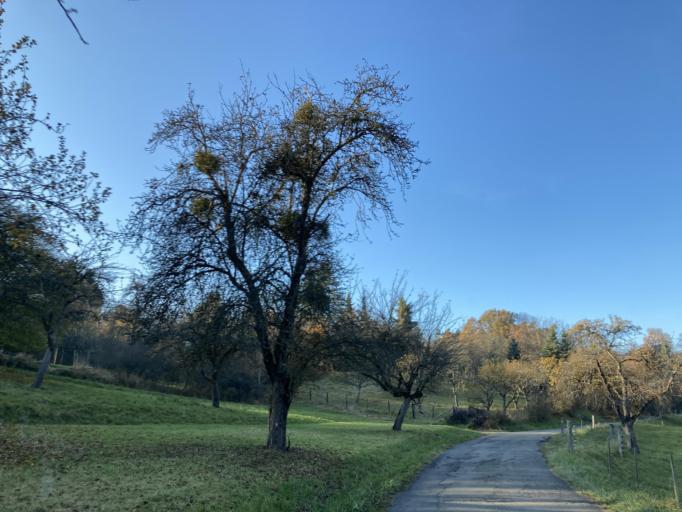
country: DE
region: Baden-Wuerttemberg
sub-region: Tuebingen Region
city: Rottenburg
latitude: 48.5370
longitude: 8.9777
